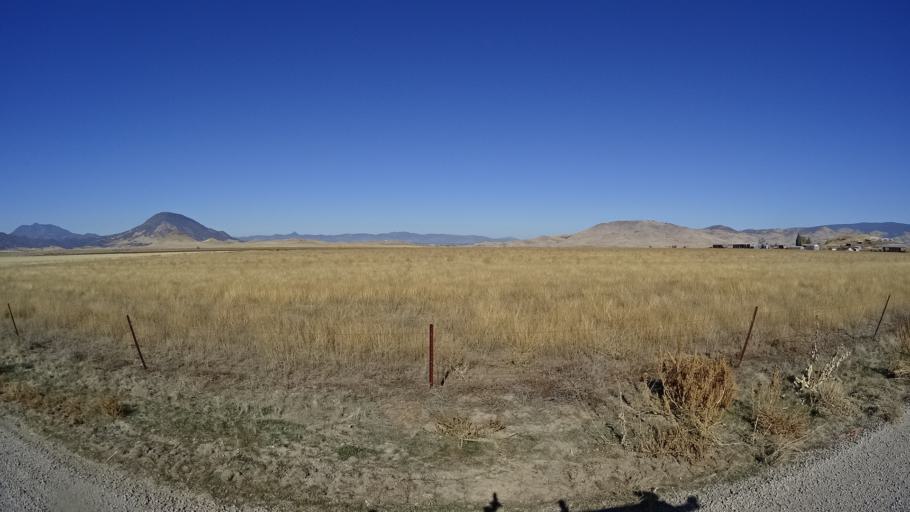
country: US
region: California
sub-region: Siskiyou County
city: Montague
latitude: 41.7865
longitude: -122.4401
